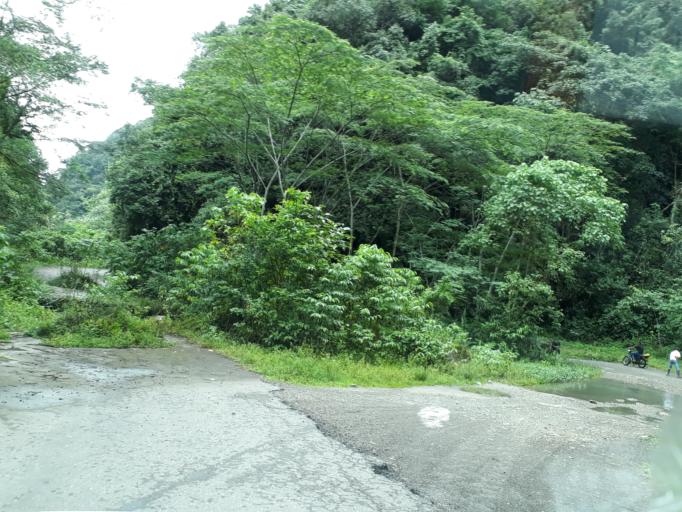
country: CO
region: Boyaca
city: Santa Maria
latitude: 4.7316
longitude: -73.3072
